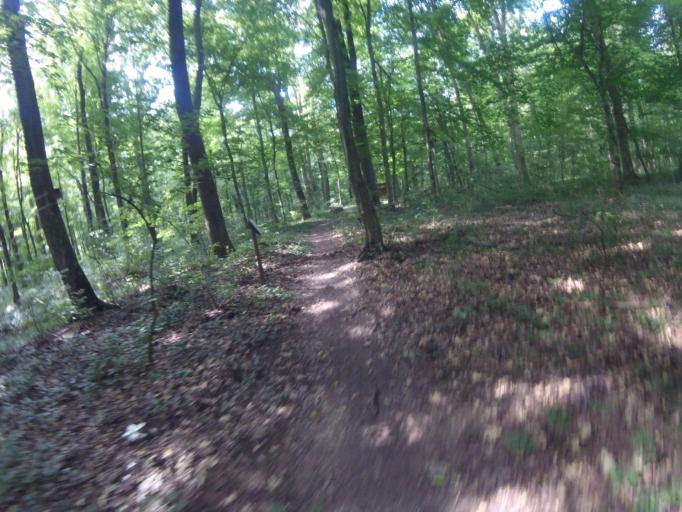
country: HU
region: Zala
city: Lenti
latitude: 46.6284
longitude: 16.5538
